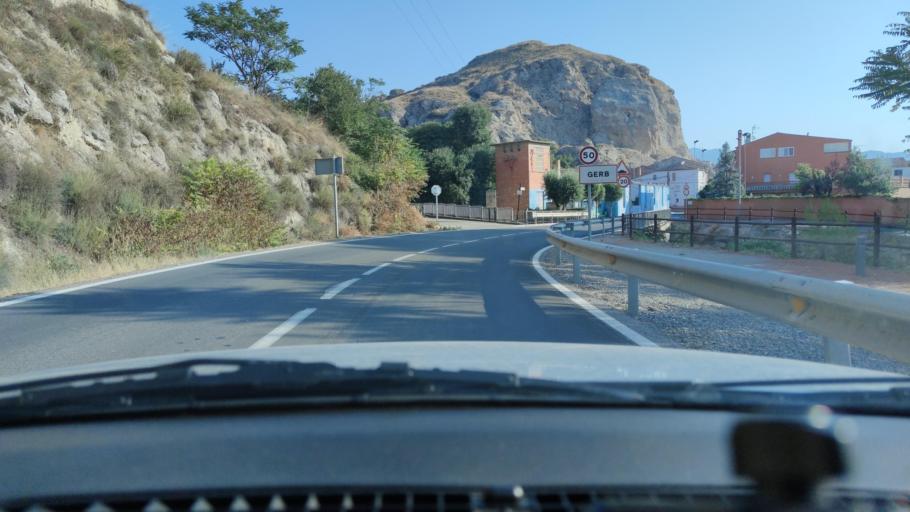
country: ES
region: Catalonia
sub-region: Provincia de Lleida
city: Balaguer
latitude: 41.8212
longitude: 0.8030
